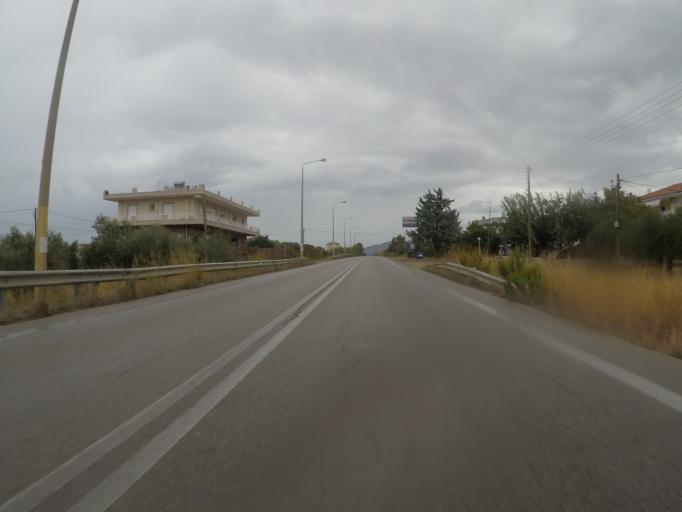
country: GR
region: West Greece
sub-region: Nomos Ileias
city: Zacharo
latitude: 37.4219
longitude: 21.6689
